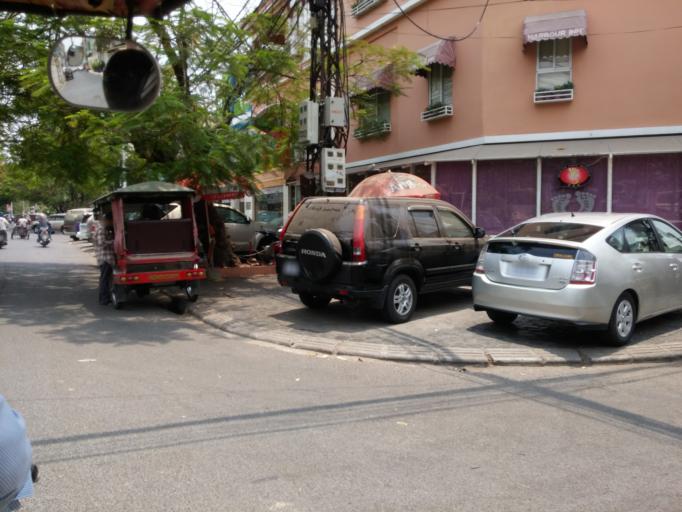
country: KH
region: Phnom Penh
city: Phnom Penh
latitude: 11.5598
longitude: 104.9186
